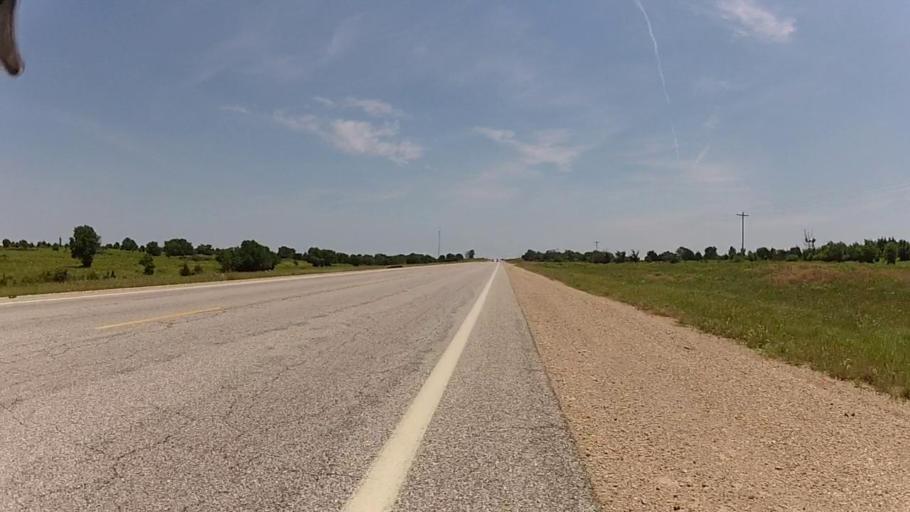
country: US
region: Kansas
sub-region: Chautauqua County
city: Sedan
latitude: 37.1132
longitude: -96.3246
